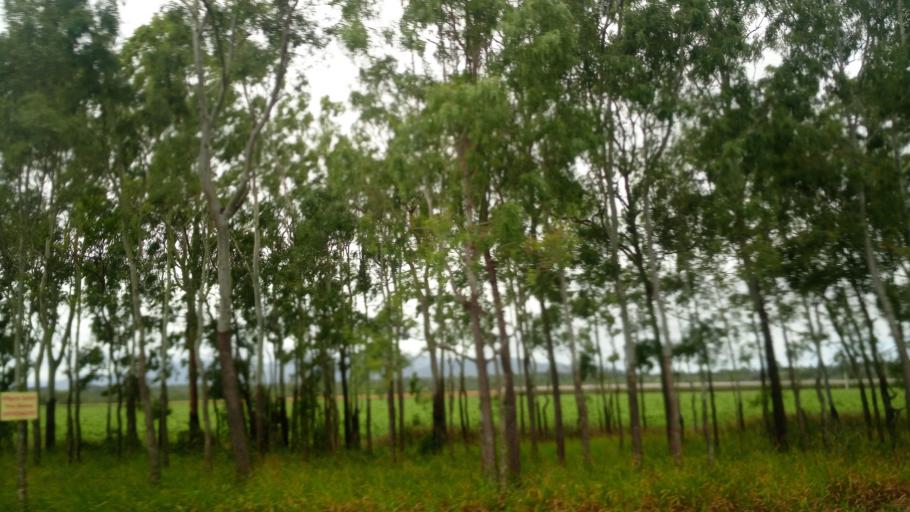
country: AU
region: Queensland
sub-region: Tablelands
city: Tolga
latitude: -17.1764
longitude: 145.4450
